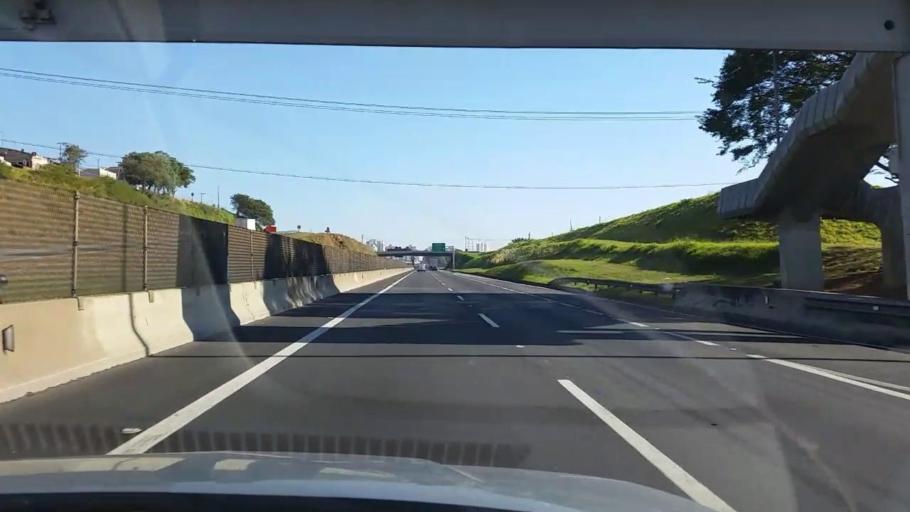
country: BR
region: Sao Paulo
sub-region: Jundiai
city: Jundiai
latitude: -23.2207
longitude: -46.8797
